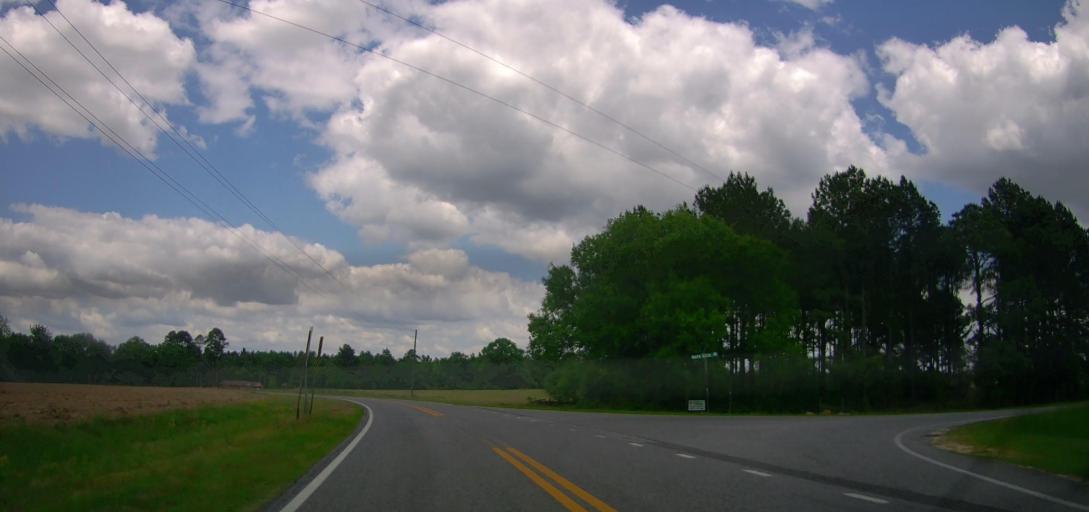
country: US
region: Georgia
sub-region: Laurens County
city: East Dublin
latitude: 32.5371
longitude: -82.8100
